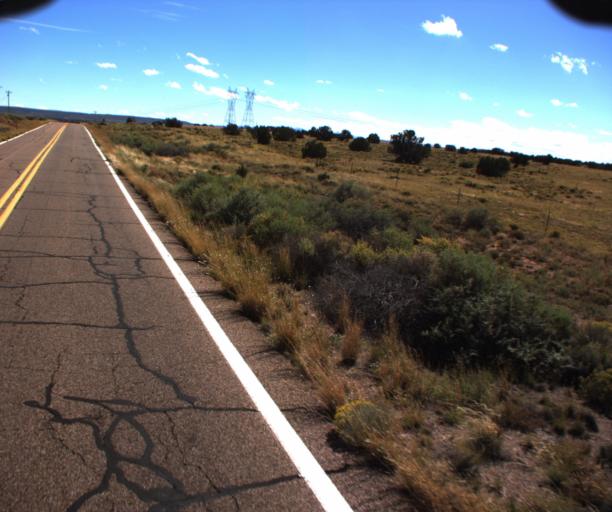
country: US
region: Arizona
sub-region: Apache County
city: Saint Johns
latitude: 34.5586
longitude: -109.6278
